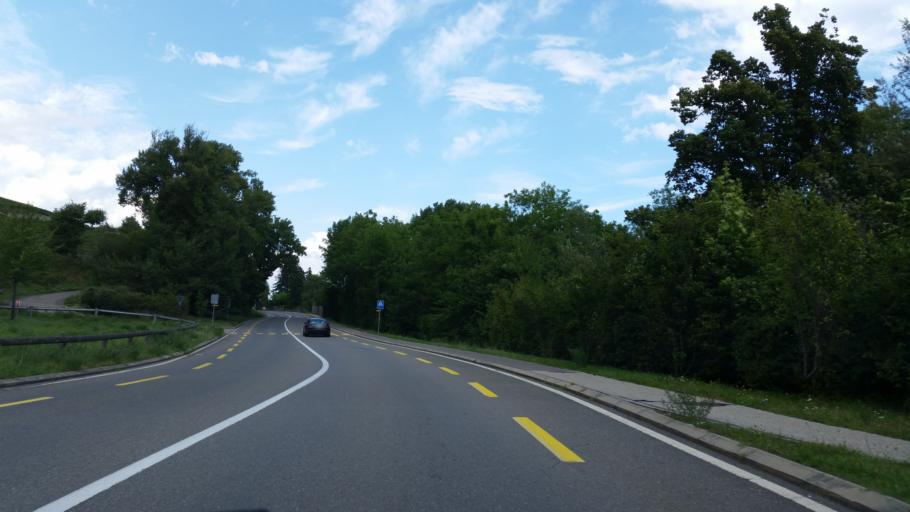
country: CH
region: Neuchatel
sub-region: Boudry District
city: Saint-Aubin-Sauges
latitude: 46.8789
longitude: 6.7599
